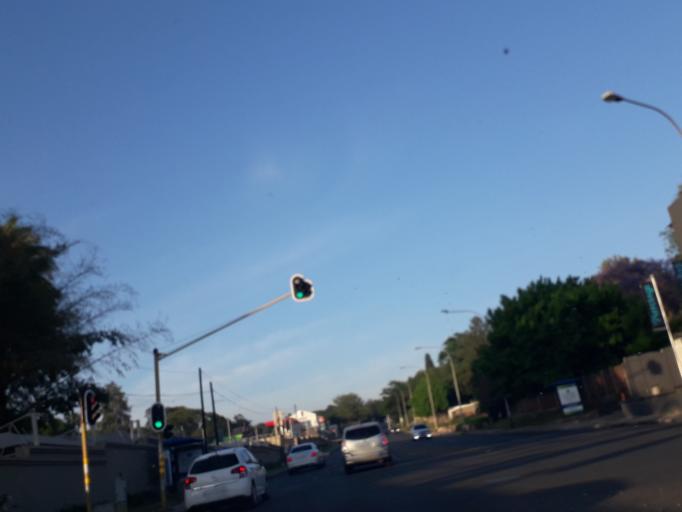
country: ZA
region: Gauteng
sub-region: City of Johannesburg Metropolitan Municipality
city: Modderfontein
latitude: -26.1315
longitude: 28.0995
